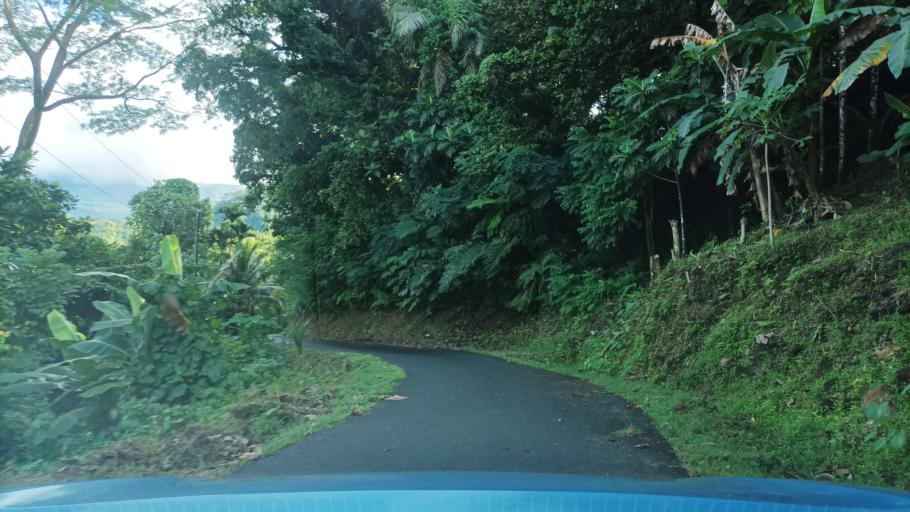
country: FM
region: Pohnpei
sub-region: Kolonia Municipality
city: Kolonia Town
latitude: 6.9626
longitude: 158.1941
